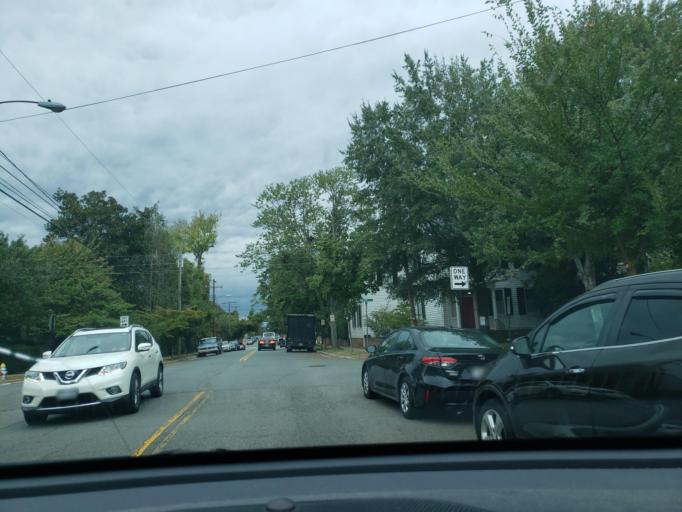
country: US
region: Virginia
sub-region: City of Fredericksburg
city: Fredericksburg
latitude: 38.3004
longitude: -77.4614
